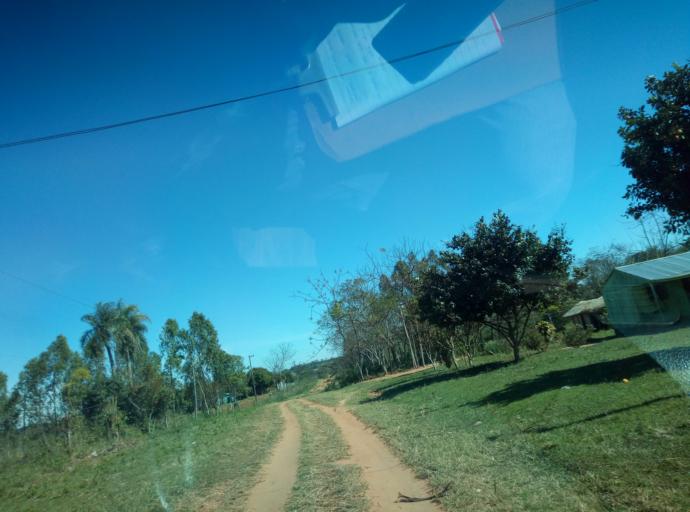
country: PY
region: Caaguazu
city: Doctor Cecilio Baez
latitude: -25.1789
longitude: -56.2460
